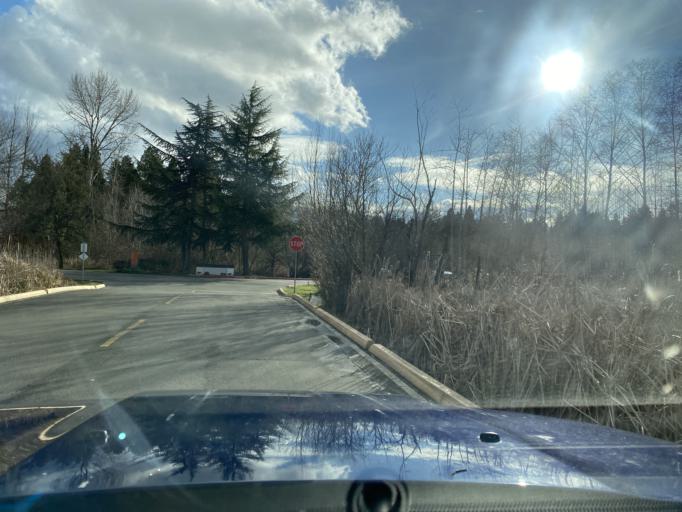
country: US
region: Washington
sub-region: King County
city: Bellevue
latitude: 47.5956
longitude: -122.1908
